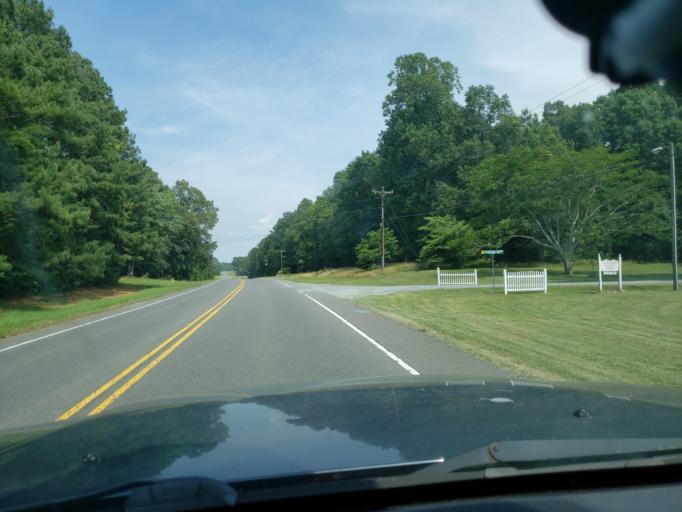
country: US
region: North Carolina
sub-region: Alamance County
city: Saxapahaw
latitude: 35.9333
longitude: -79.2237
